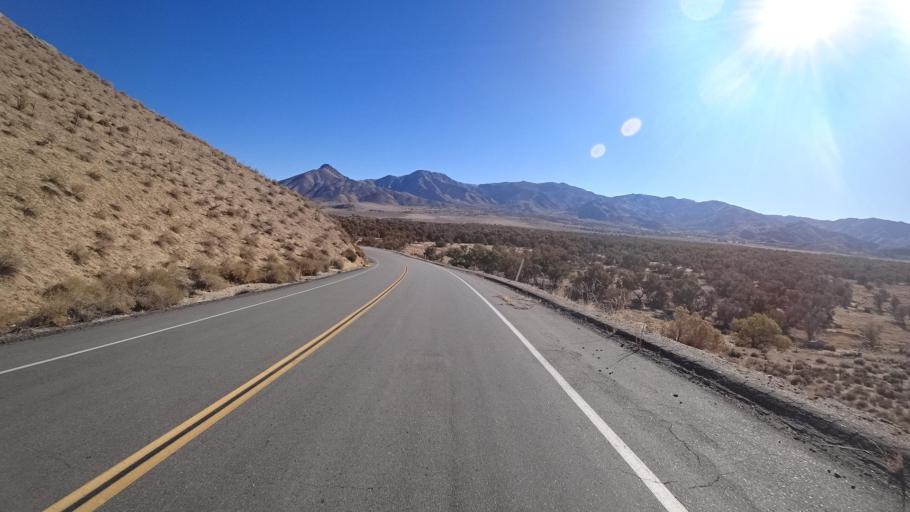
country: US
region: California
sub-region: Kern County
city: Weldon
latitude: 35.6747
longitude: -118.3561
